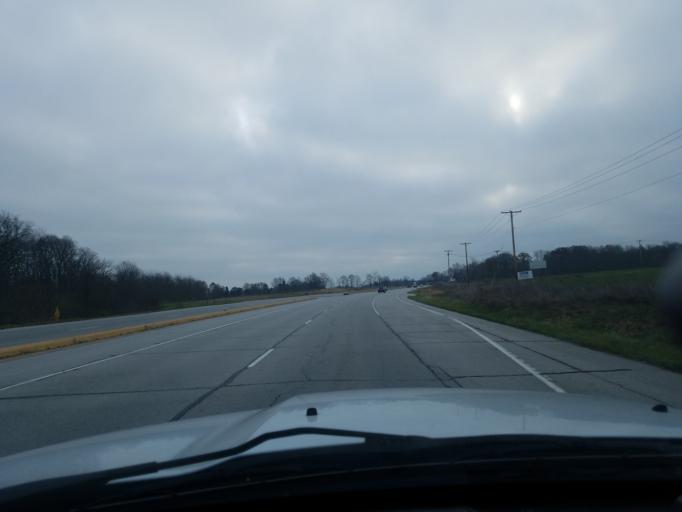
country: US
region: Indiana
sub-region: Delaware County
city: Yorktown
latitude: 40.2187
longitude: -85.5542
